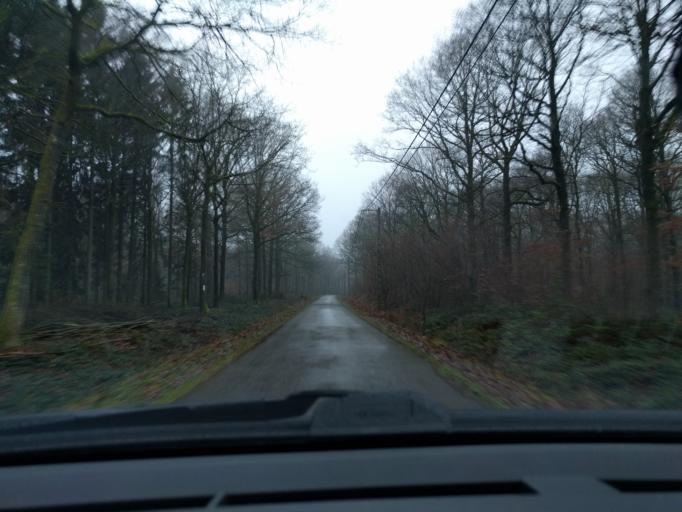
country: BE
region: Wallonia
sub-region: Province de Namur
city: Couvin
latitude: 50.0435
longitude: 4.5267
